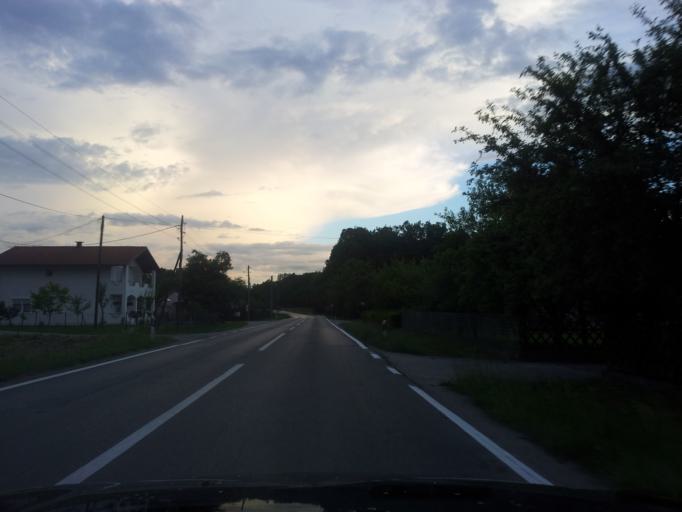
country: HR
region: Karlovacka
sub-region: Grad Karlovac
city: Karlovac
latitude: 45.5457
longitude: 15.5698
